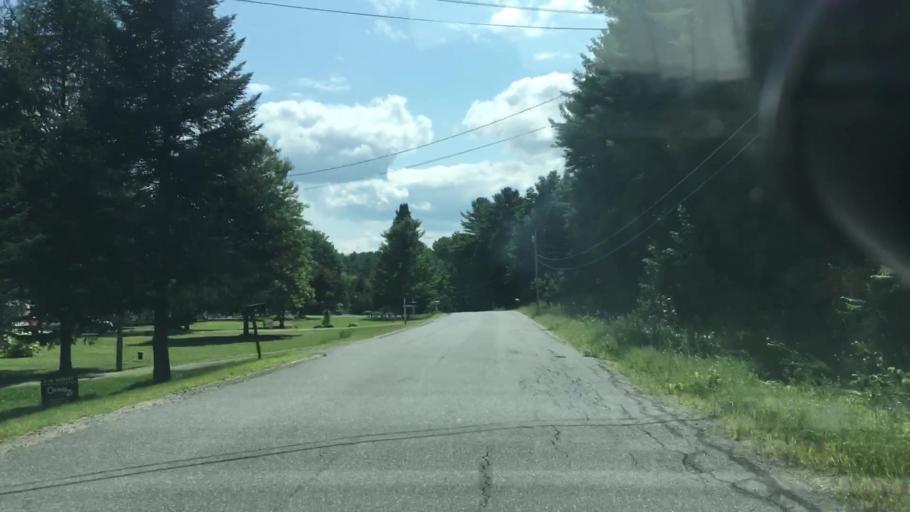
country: US
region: Maine
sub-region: Somerset County
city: Skowhegan
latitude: 44.6783
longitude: -69.6866
